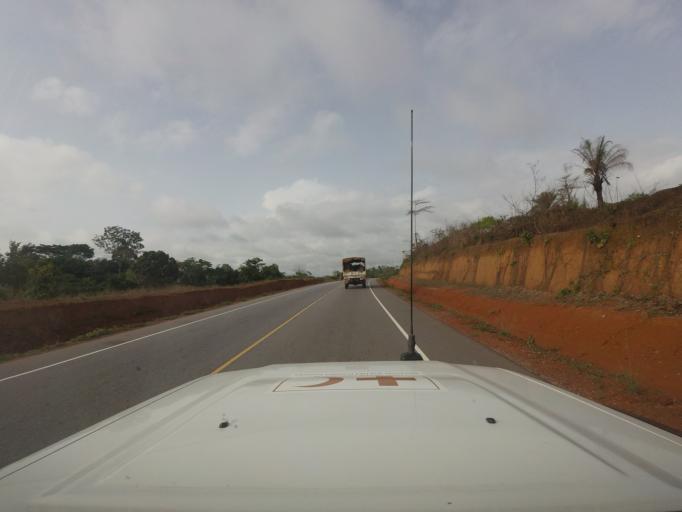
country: LR
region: Bong
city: Gbarnga
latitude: 7.0127
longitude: -9.2789
